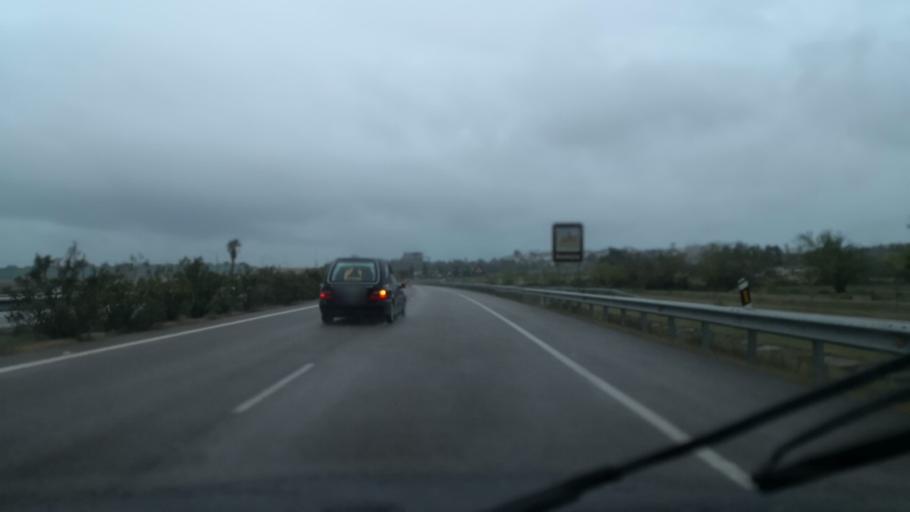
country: ES
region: Extremadura
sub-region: Provincia de Badajoz
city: Badajoz
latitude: 38.9035
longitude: -6.9673
